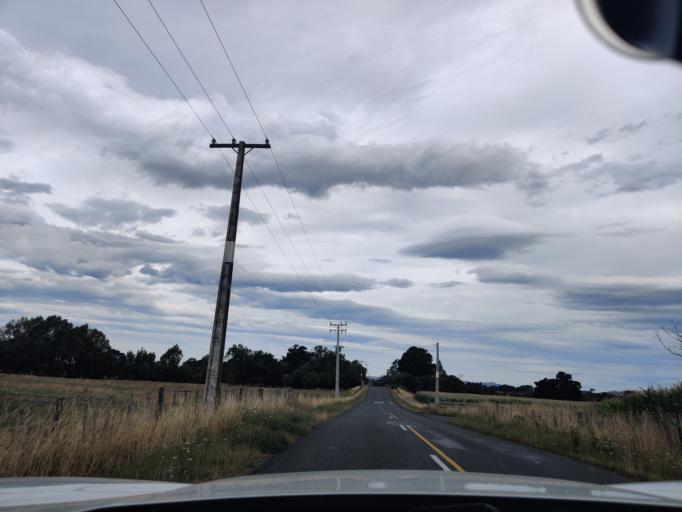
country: NZ
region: Wellington
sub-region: Masterton District
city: Masterton
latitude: -41.0369
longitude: 175.4960
